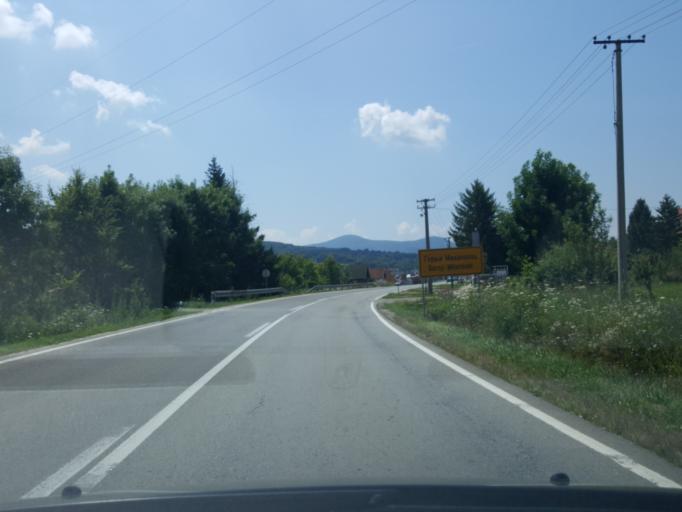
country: RS
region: Central Serbia
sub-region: Moravicki Okrug
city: Gornji Milanovac
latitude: 44.0466
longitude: 20.4879
